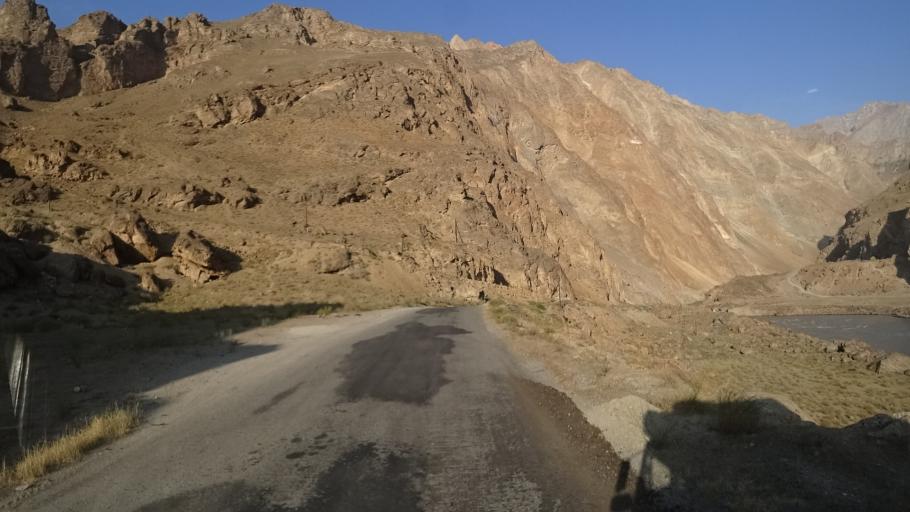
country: TJ
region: Gorno-Badakhshan
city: Vanj
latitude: 38.2725
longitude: 71.3481
